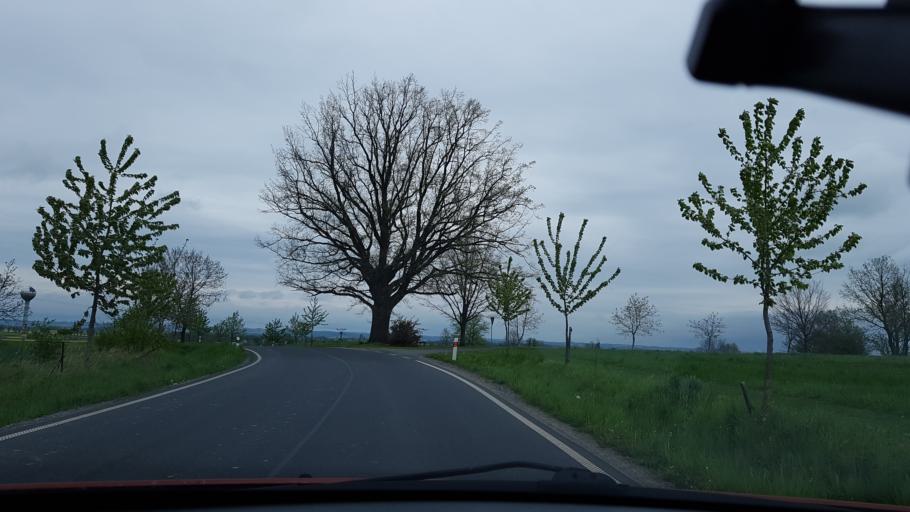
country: CZ
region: Olomoucky
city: Javornik
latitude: 50.3896
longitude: 17.0738
